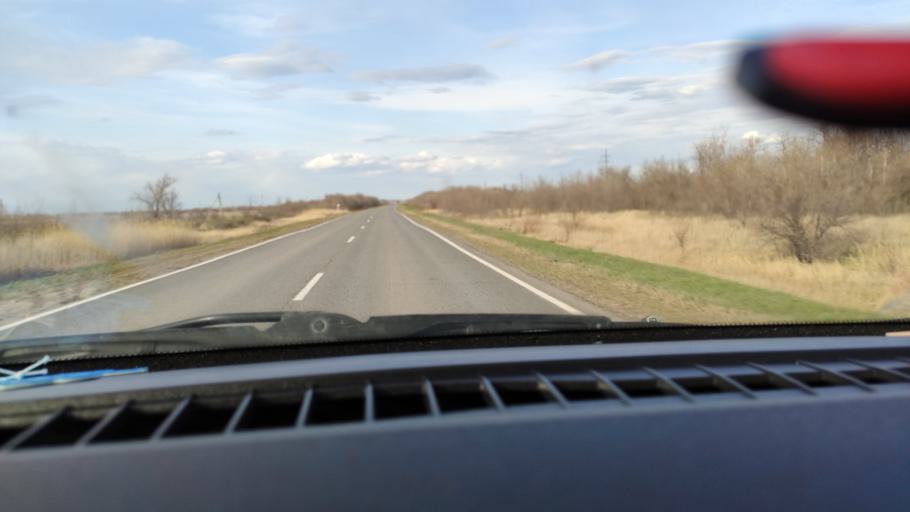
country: RU
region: Saratov
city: Privolzhskiy
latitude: 51.3183
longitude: 46.0220
